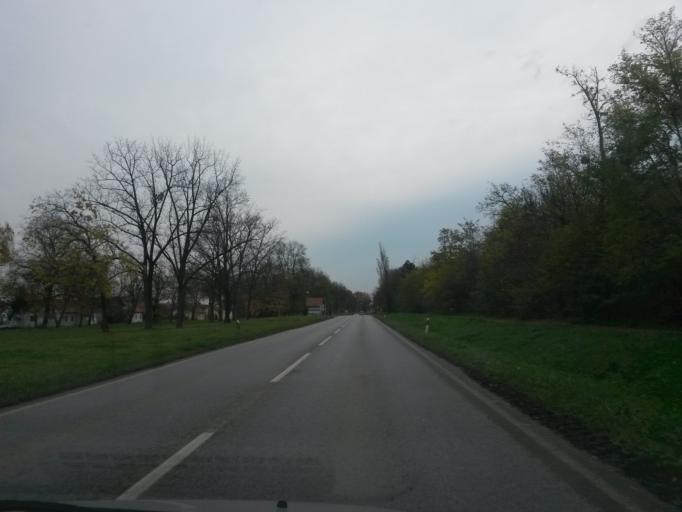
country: HR
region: Osjecko-Baranjska
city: Darda
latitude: 45.6214
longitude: 18.7159
